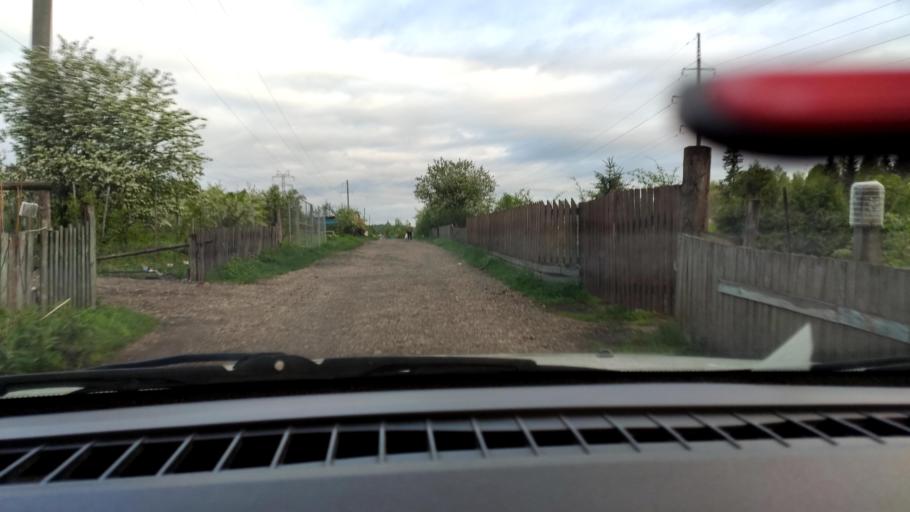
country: RU
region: Perm
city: Polazna
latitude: 58.1332
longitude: 56.4105
